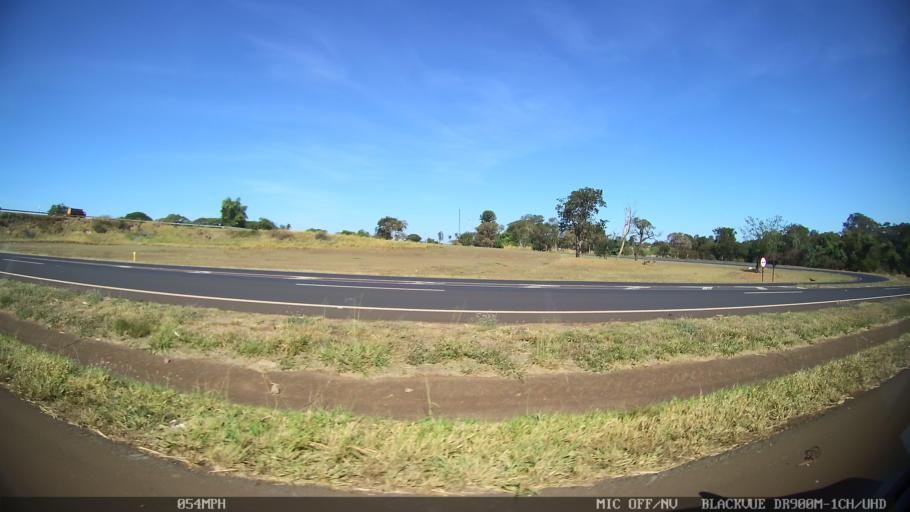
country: BR
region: Sao Paulo
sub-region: Barretos
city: Barretos
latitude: -20.5326
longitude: -48.6003
